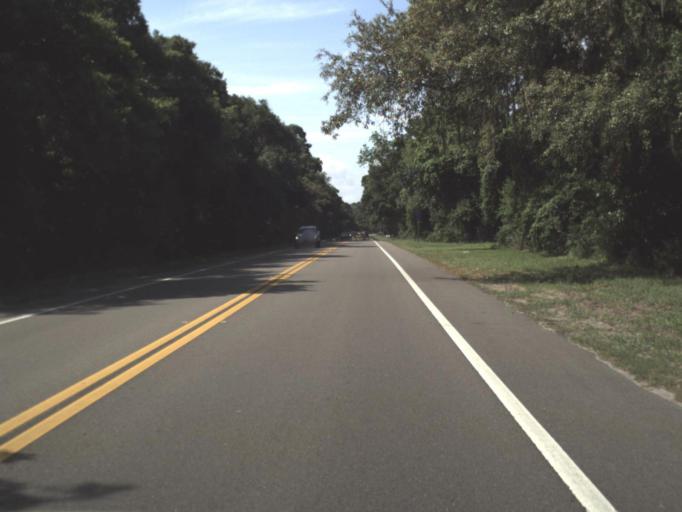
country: US
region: Florida
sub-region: Nassau County
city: Fernandina Beach
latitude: 30.5595
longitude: -81.4510
